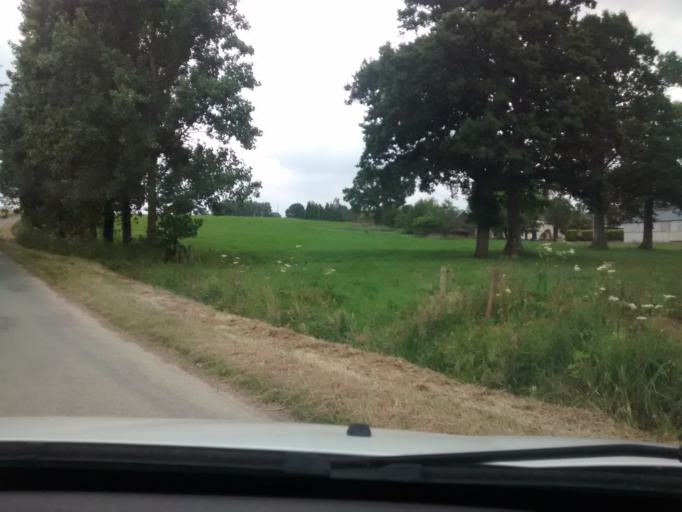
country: FR
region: Brittany
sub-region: Departement d'Ille-et-Vilaine
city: Noyal-sur-Vilaine
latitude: 48.1281
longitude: -1.5181
